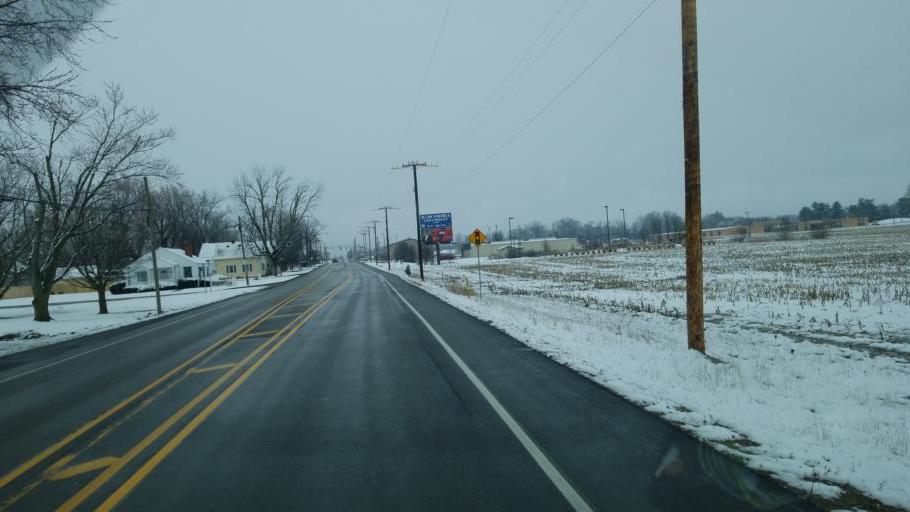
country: US
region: Indiana
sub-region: Delaware County
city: Muncie
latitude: 40.2652
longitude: -85.3681
